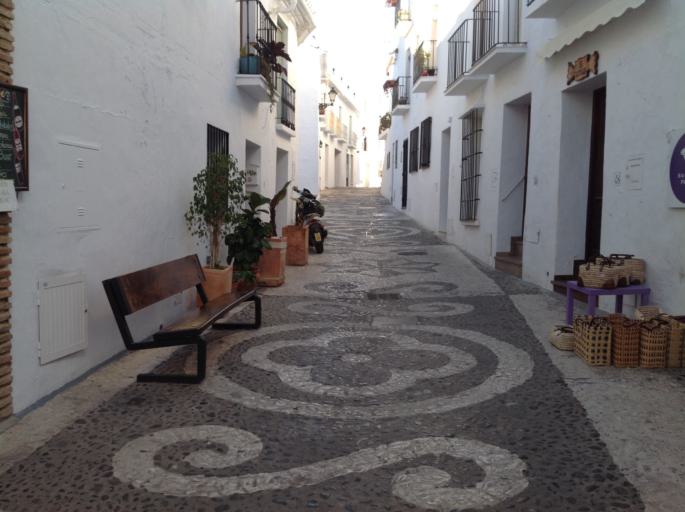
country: ES
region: Andalusia
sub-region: Provincia de Malaga
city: Frigiliana
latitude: 36.7921
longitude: -3.8970
